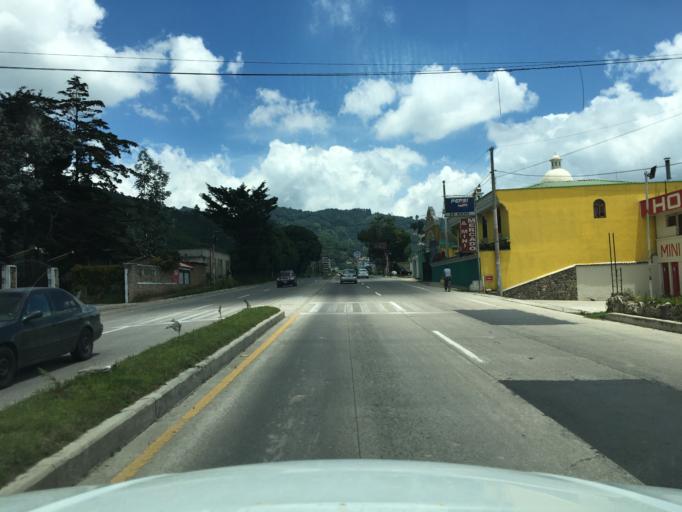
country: GT
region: Chimaltenango
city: Tecpan Guatemala
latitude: 14.7729
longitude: -90.9884
